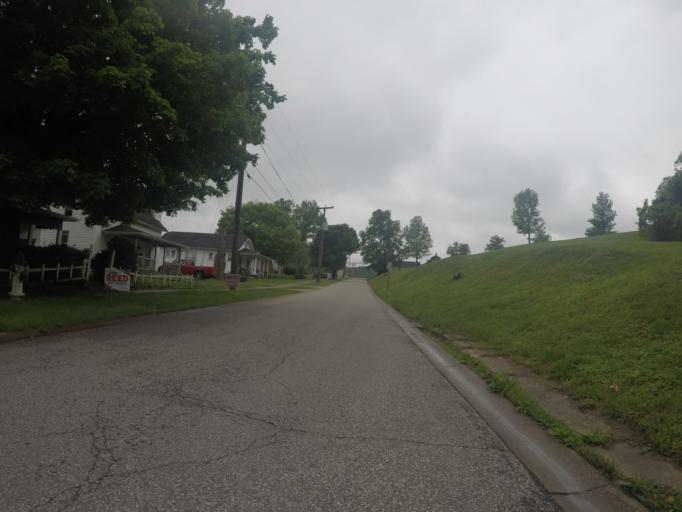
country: US
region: West Virginia
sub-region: Cabell County
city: Barboursville
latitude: 38.4107
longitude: -82.2935
